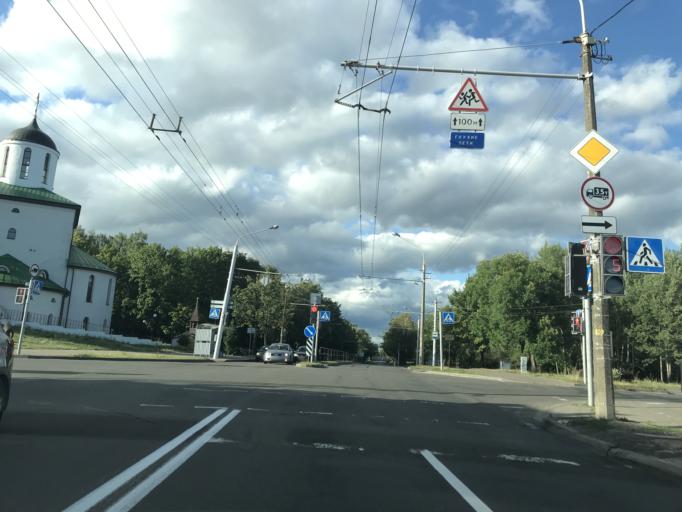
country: BY
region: Minsk
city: Minsk
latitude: 53.9396
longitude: 27.6167
